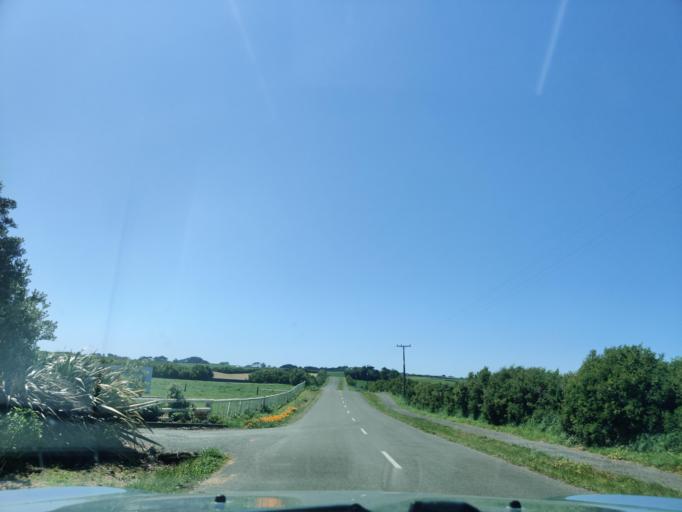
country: NZ
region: Taranaki
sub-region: South Taranaki District
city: Hawera
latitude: -39.6032
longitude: 174.2461
